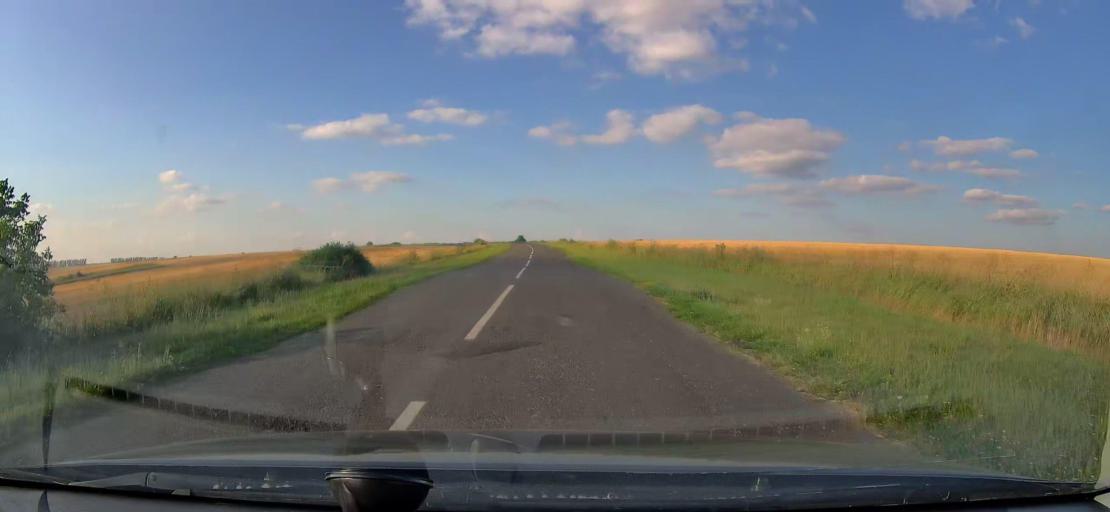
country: RU
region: Kursk
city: Zolotukhino
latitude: 52.0310
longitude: 36.2166
